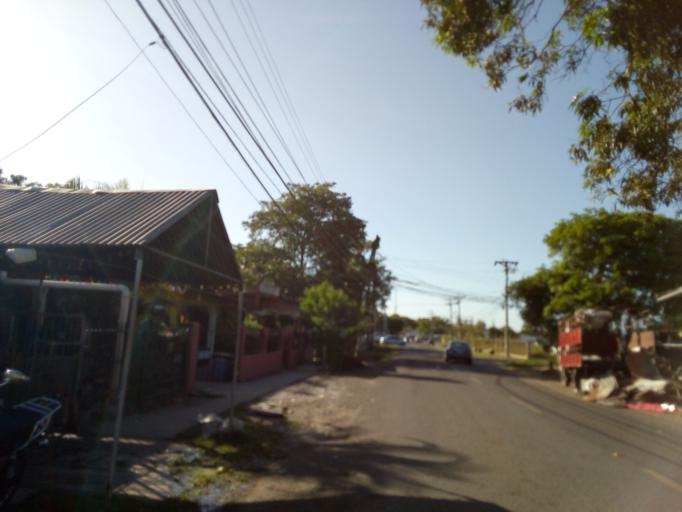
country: PA
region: Veraguas
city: Santiago de Veraguas
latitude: 8.1103
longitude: -80.9687
